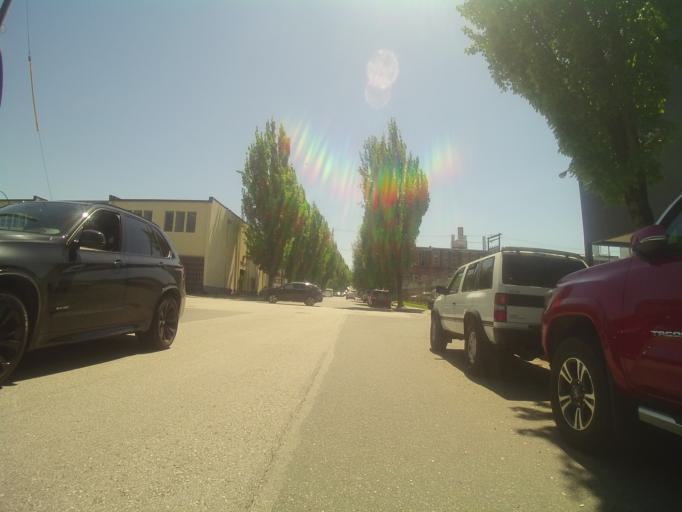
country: CA
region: British Columbia
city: Vancouver
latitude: 49.2685
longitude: -123.1047
